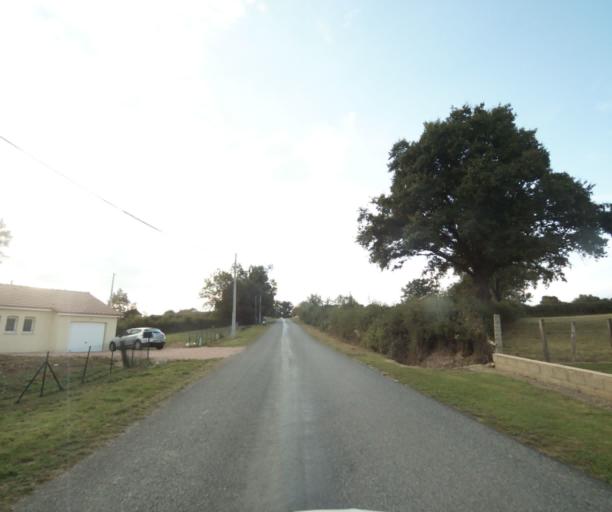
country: FR
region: Bourgogne
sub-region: Departement de Saone-et-Loire
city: Charolles
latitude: 46.4469
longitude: 4.3336
